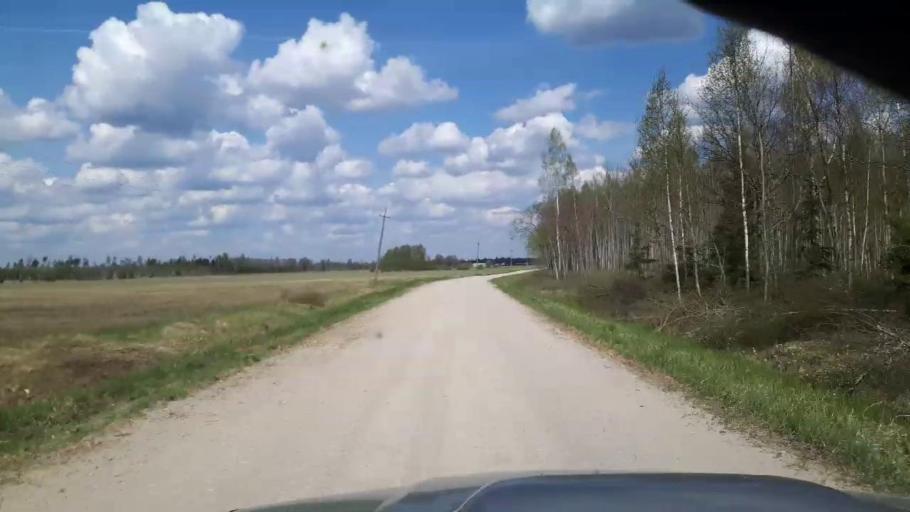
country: EE
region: Paernumaa
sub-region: Tootsi vald
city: Tootsi
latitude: 58.4775
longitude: 24.9024
